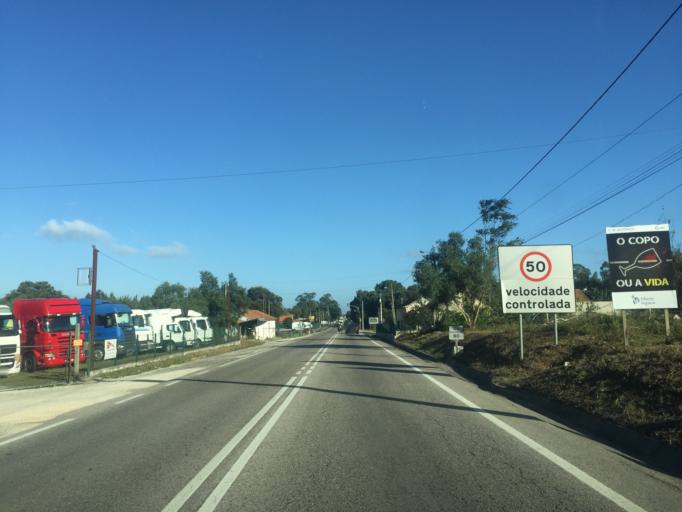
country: PT
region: Leiria
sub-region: Alcobaca
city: Benedita
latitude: 39.3945
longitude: -8.9598
